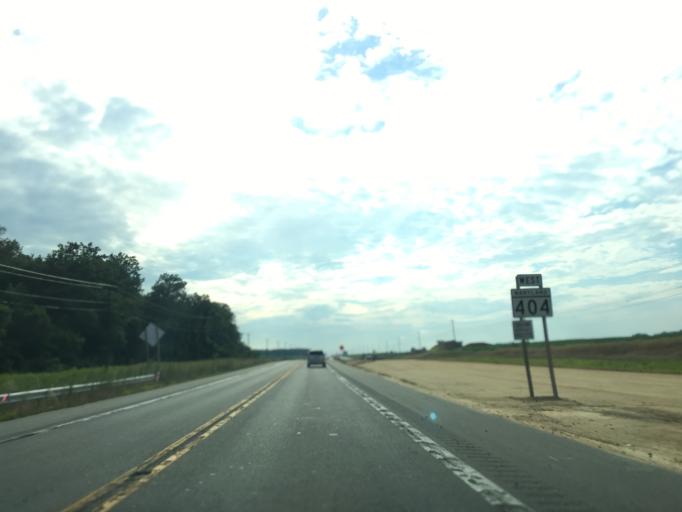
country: US
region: Maryland
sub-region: Caroline County
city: Ridgely
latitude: 38.9250
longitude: -75.9848
